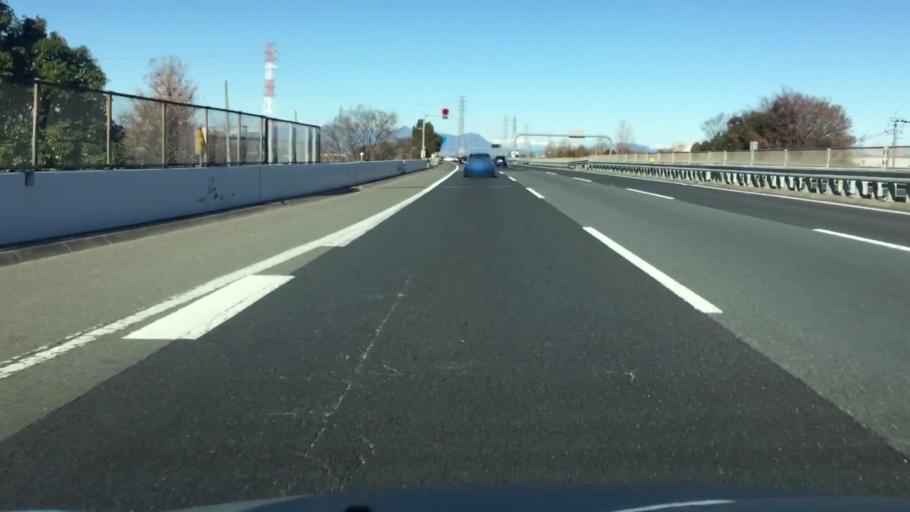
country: JP
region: Saitama
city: Honjo
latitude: 36.2205
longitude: 139.1629
